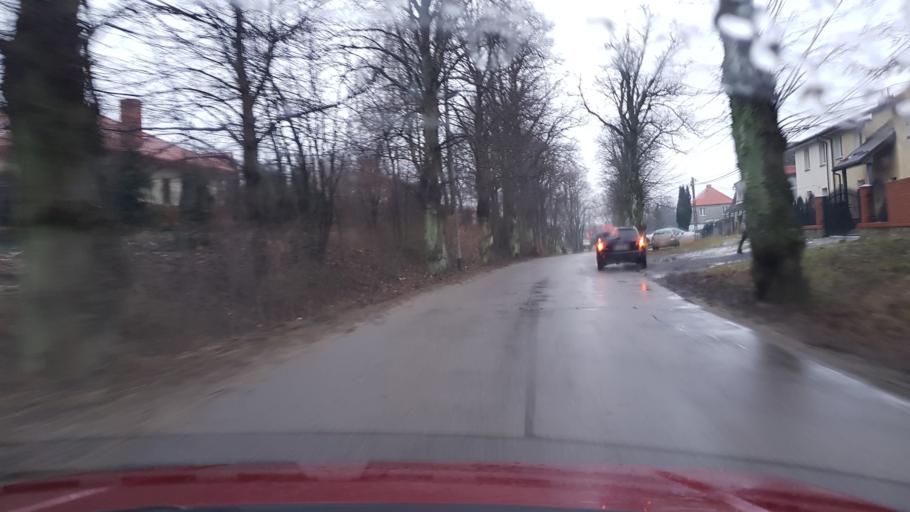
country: PL
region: West Pomeranian Voivodeship
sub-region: Powiat koszalinski
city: Sianow
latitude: 54.1835
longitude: 16.2449
